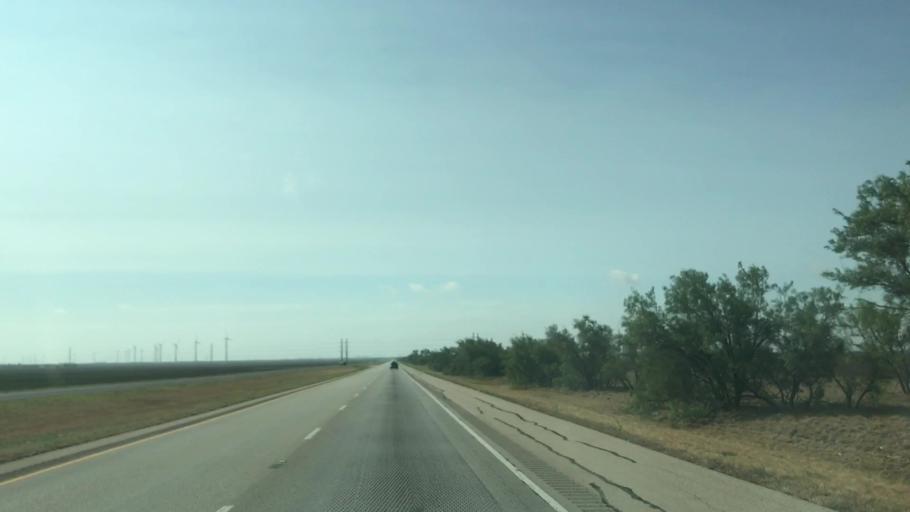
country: US
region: Texas
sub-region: Scurry County
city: Snyder
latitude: 32.6045
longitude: -100.7424
